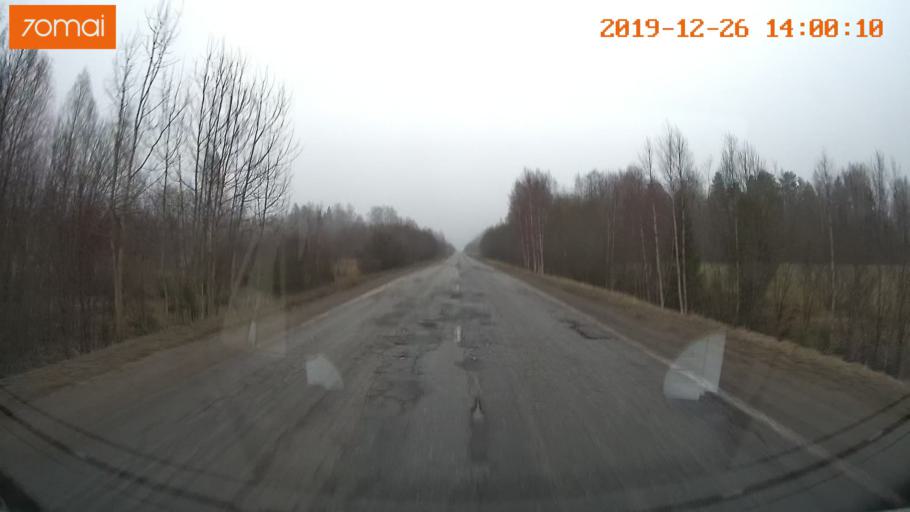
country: RU
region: Jaroslavl
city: Poshekhon'ye
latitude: 58.5601
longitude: 38.7384
